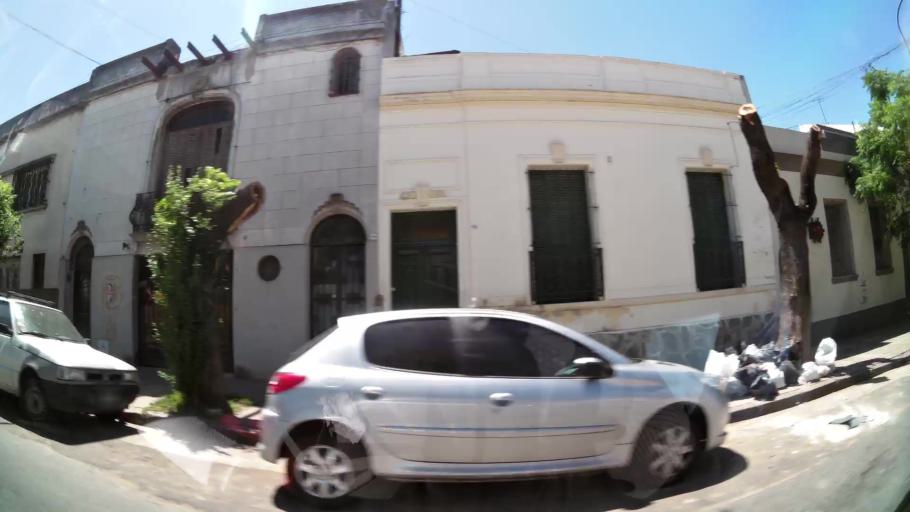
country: AR
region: Buenos Aires F.D.
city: Buenos Aires
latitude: -34.6409
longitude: -58.4090
